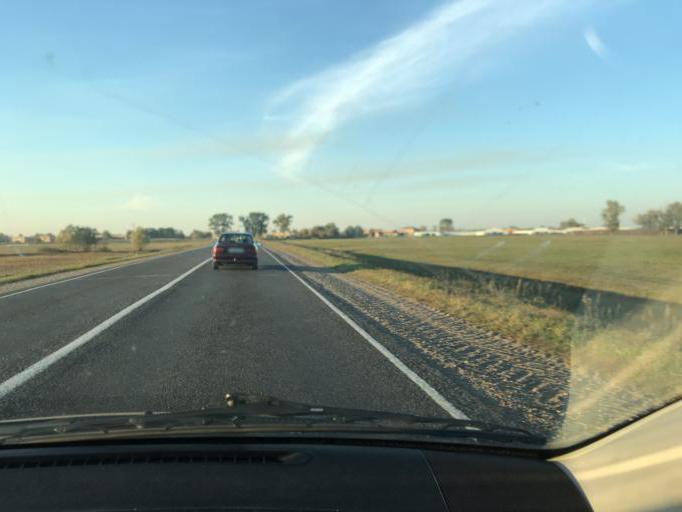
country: BY
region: Brest
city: Pinsk
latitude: 52.0593
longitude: 26.2112
